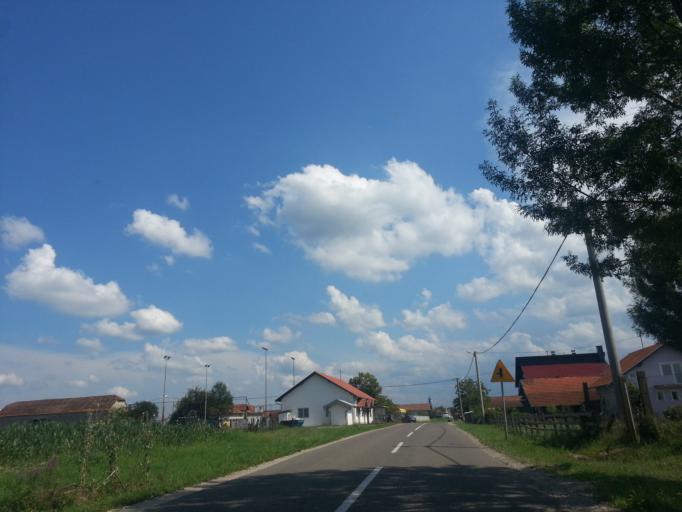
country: BA
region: Brcko
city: Brcko
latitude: 44.8282
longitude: 18.8353
